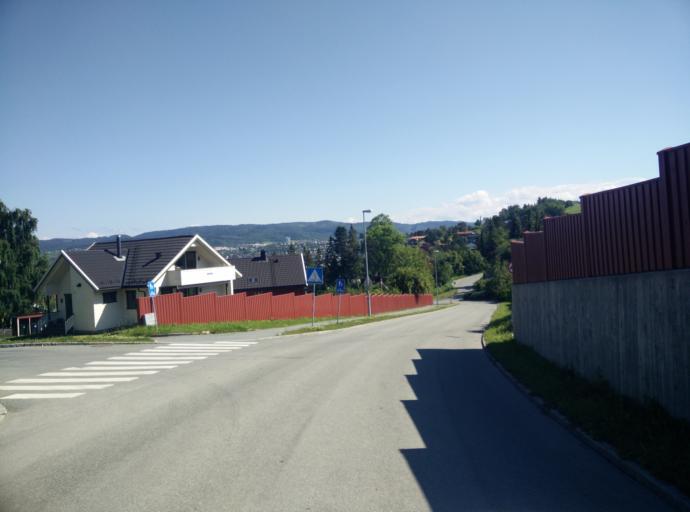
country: NO
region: Sor-Trondelag
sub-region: Trondheim
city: Trondheim
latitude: 63.4139
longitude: 10.3710
